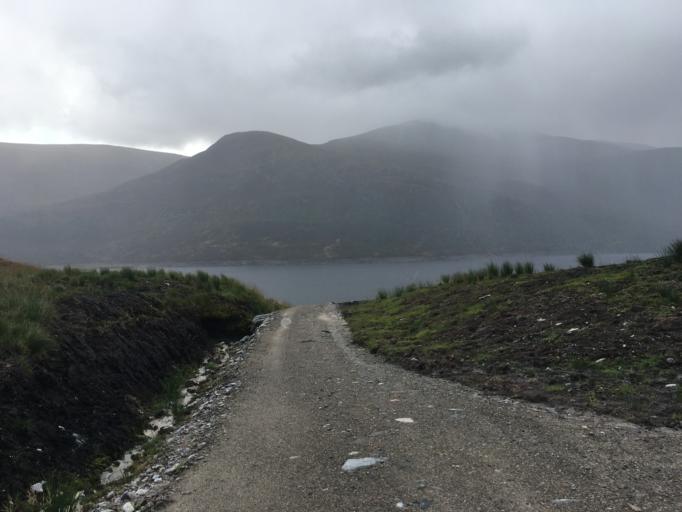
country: GB
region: Scotland
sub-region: Highland
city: Spean Bridge
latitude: 57.3441
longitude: -4.9821
